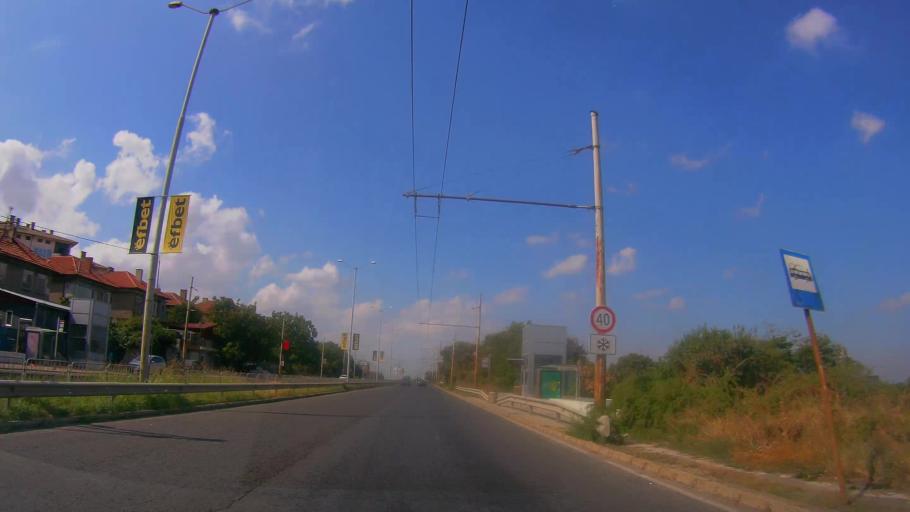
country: BG
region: Ruse
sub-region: Obshtina Ruse
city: Ruse
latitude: 43.8342
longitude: 25.9623
